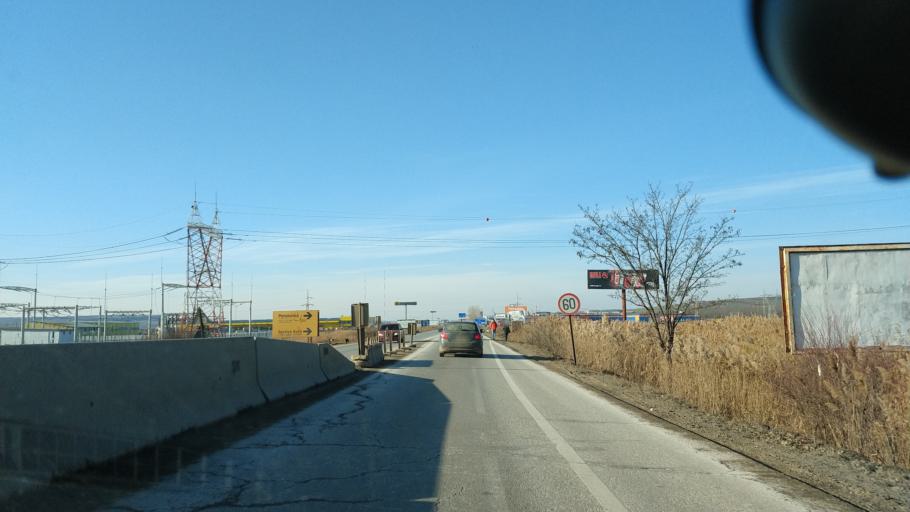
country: RO
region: Iasi
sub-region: Comuna Valea Lupului
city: Valea Lupului
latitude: 47.1789
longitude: 27.4823
